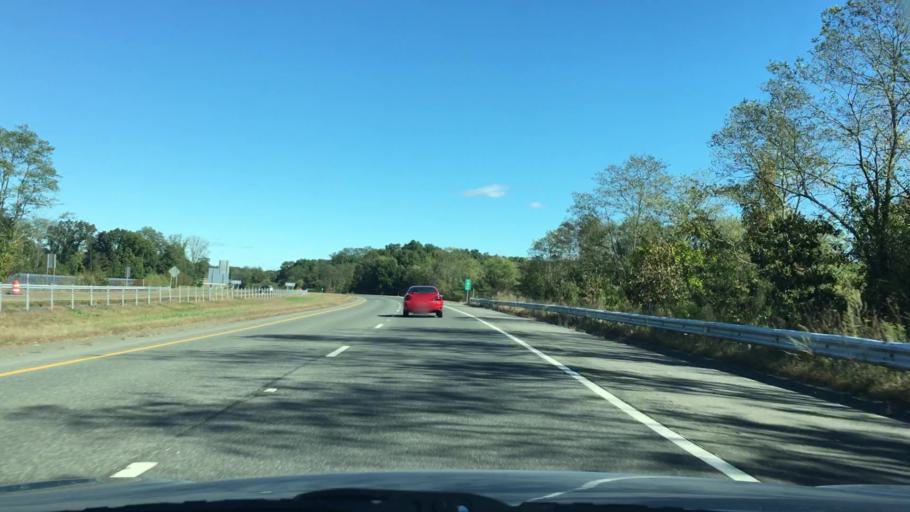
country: US
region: Massachusetts
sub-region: Hampden County
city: Agawam
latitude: 42.0579
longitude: -72.6646
